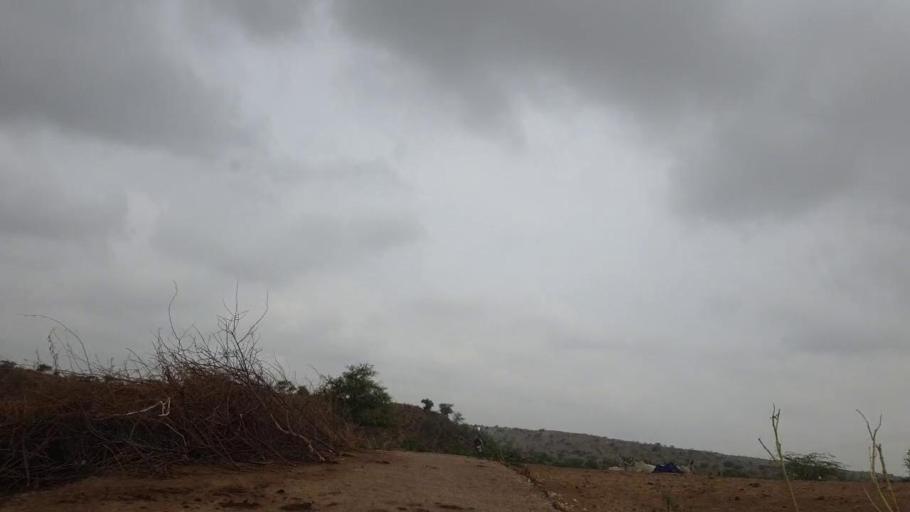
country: PK
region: Sindh
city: Diplo
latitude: 24.5125
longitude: 69.4990
